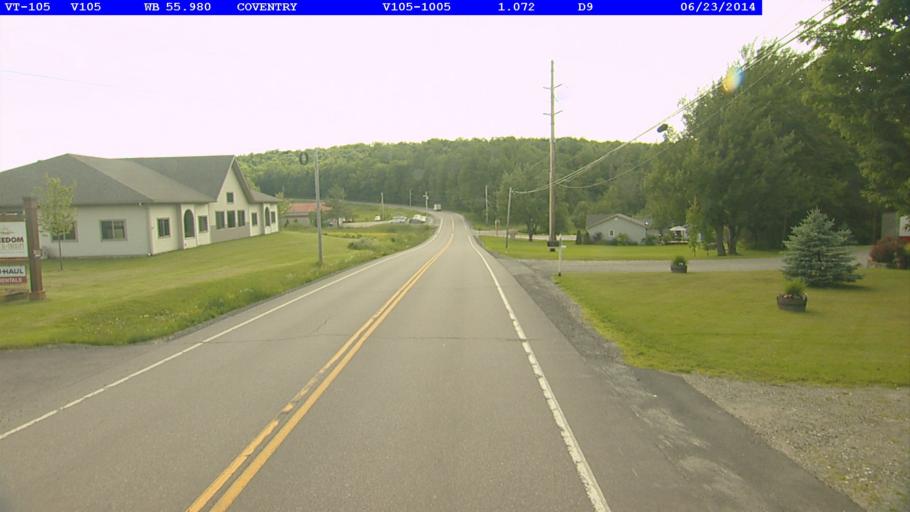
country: US
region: Vermont
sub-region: Orleans County
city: Newport
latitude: 44.9338
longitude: -72.2489
